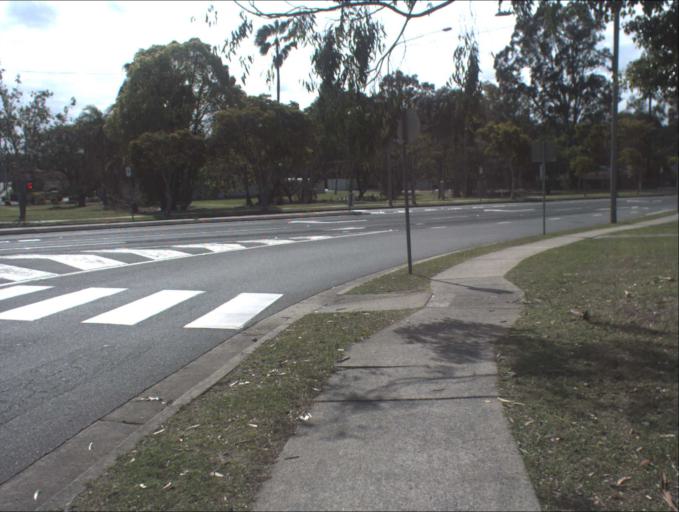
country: AU
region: Queensland
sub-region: Logan
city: Logan Reserve
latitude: -27.6806
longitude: 153.0891
